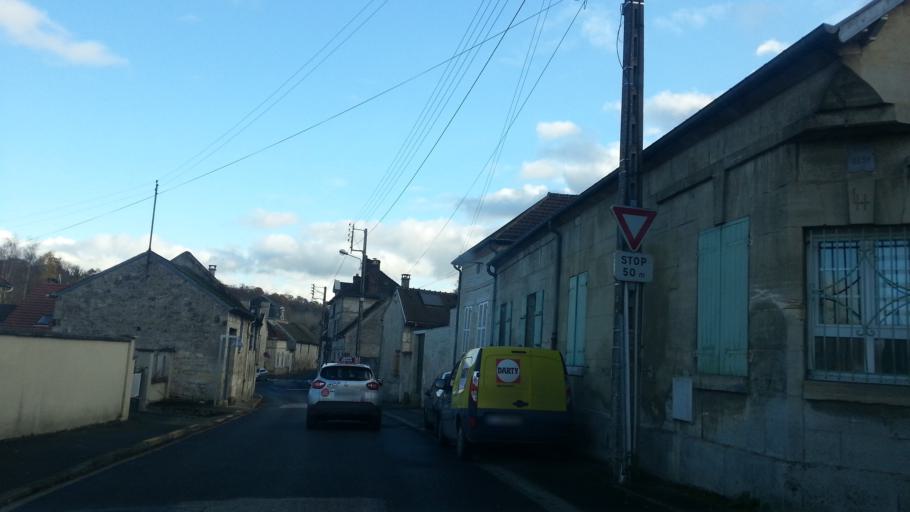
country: FR
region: Picardie
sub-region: Departement de l'Oise
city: Verneuil-en-Halatte
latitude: 49.2657
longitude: 2.5282
